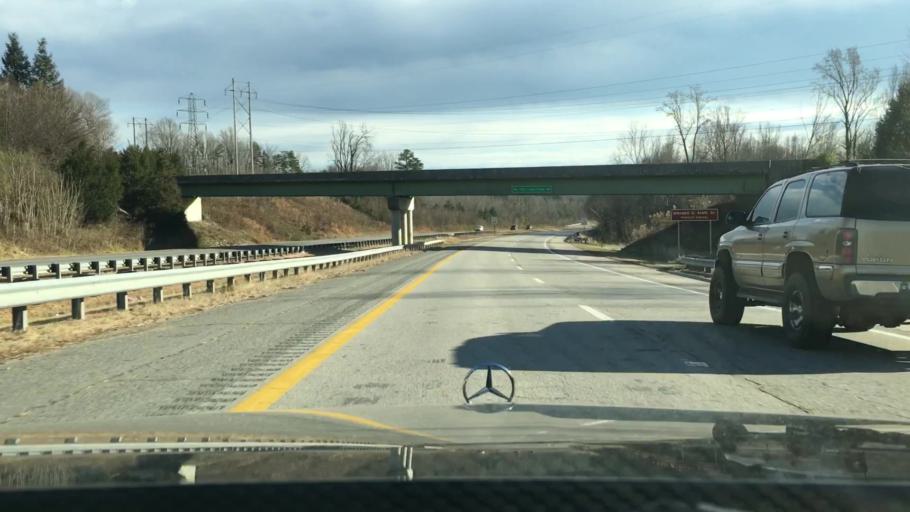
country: US
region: Virginia
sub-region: City of Danville
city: Danville
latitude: 36.6093
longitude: -79.3591
